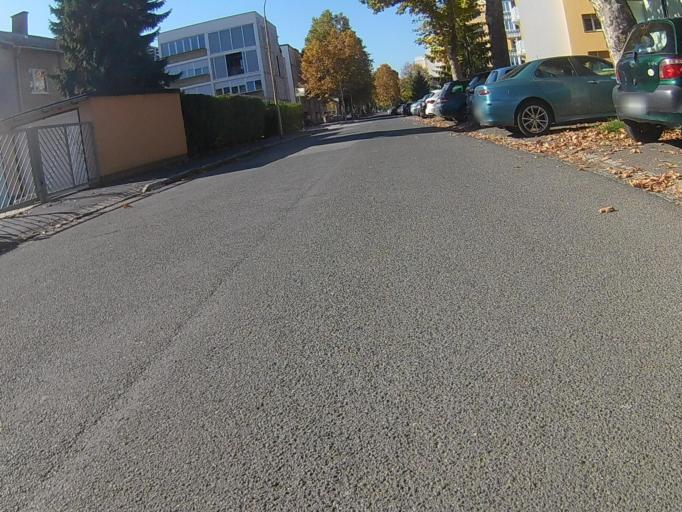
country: SI
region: Maribor
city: Maribor
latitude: 46.5656
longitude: 15.6385
